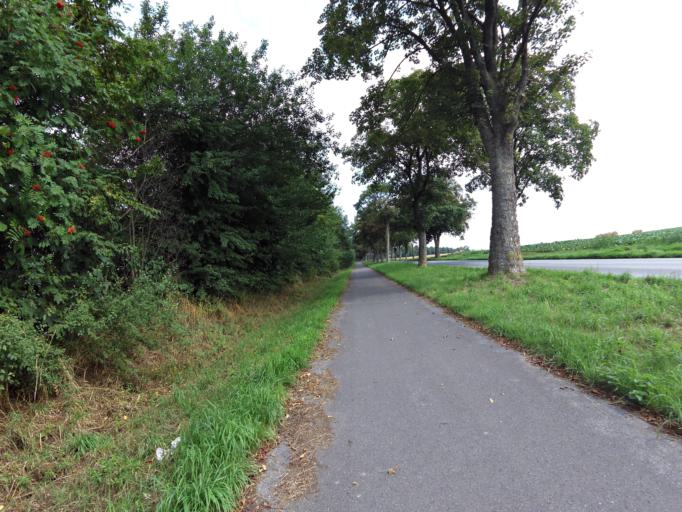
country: DE
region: North Rhine-Westphalia
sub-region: Regierungsbezirk Koln
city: Gangelt
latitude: 50.9928
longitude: 6.0391
